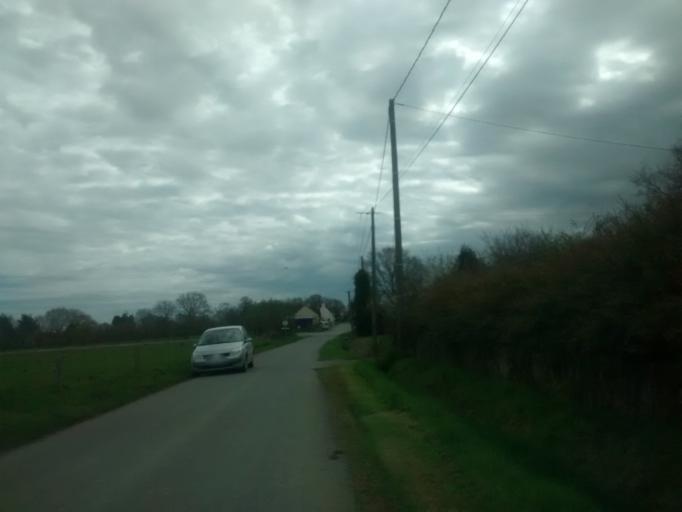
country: FR
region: Brittany
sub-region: Departement d'Ille-et-Vilaine
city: Erce-pres-Liffre
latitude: 48.2437
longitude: -1.5119
